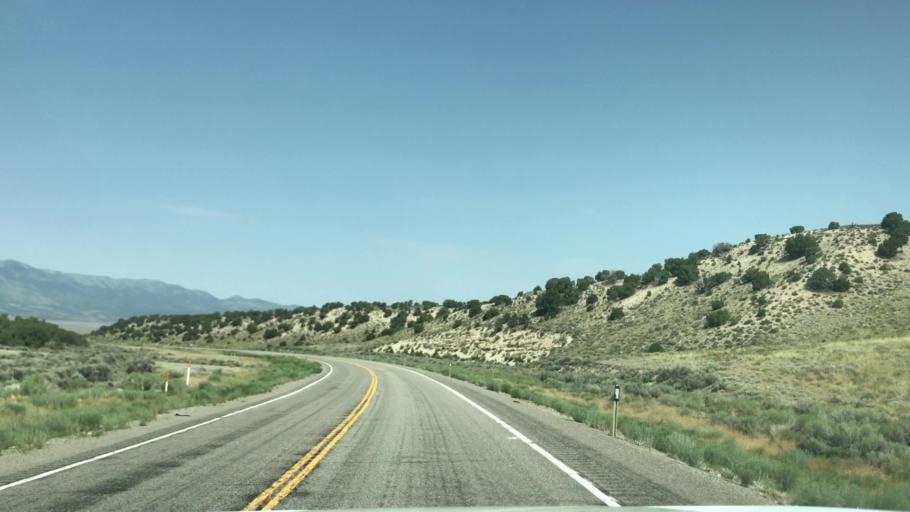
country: US
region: Nevada
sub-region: White Pine County
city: Ely
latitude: 39.0304
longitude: -114.6942
